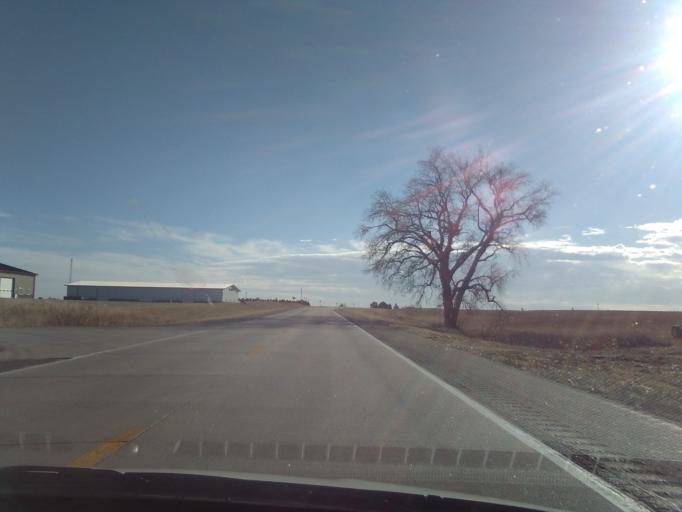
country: US
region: Nebraska
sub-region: Adams County
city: Hastings
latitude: 40.3578
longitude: -98.4396
